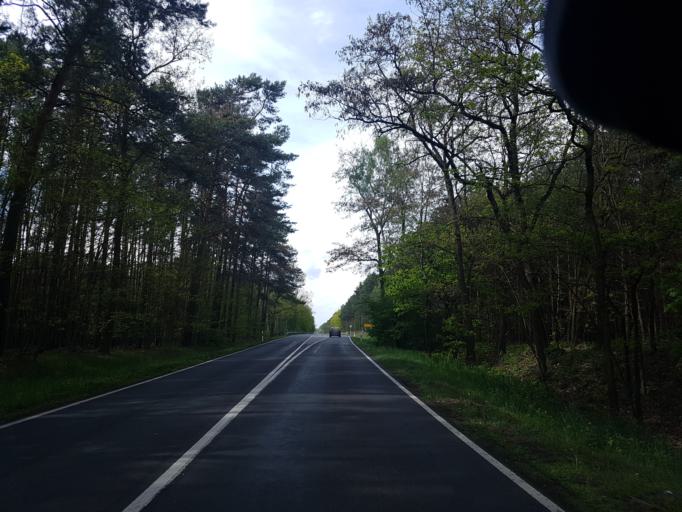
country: DE
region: Saxony
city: Gross Duben
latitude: 51.6491
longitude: 14.5387
